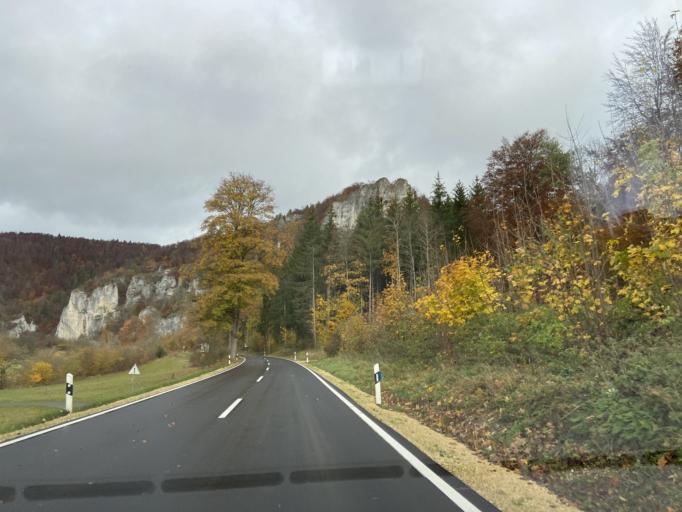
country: DE
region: Baden-Wuerttemberg
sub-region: Tuebingen Region
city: Stetten am Kalten Markt
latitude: 48.0885
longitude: 9.1084
